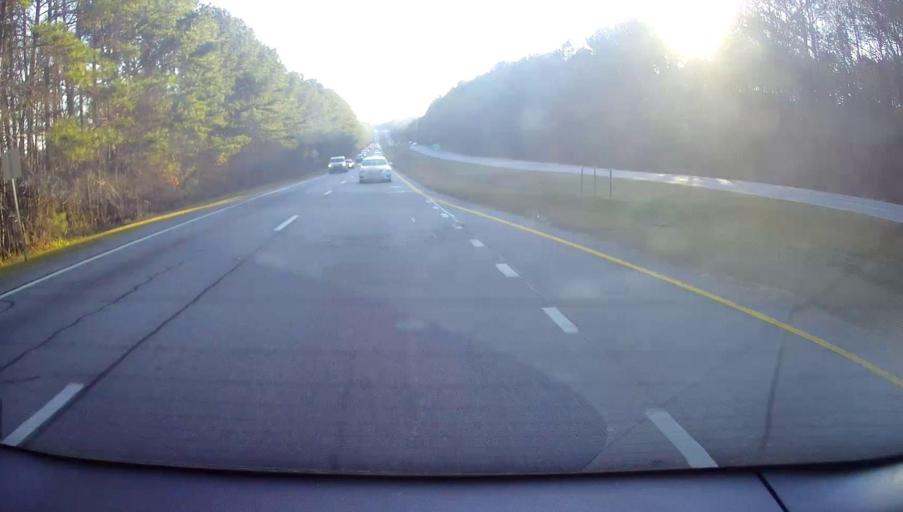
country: US
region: Georgia
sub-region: Fayette County
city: Tyrone
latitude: 33.4401
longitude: -84.5923
